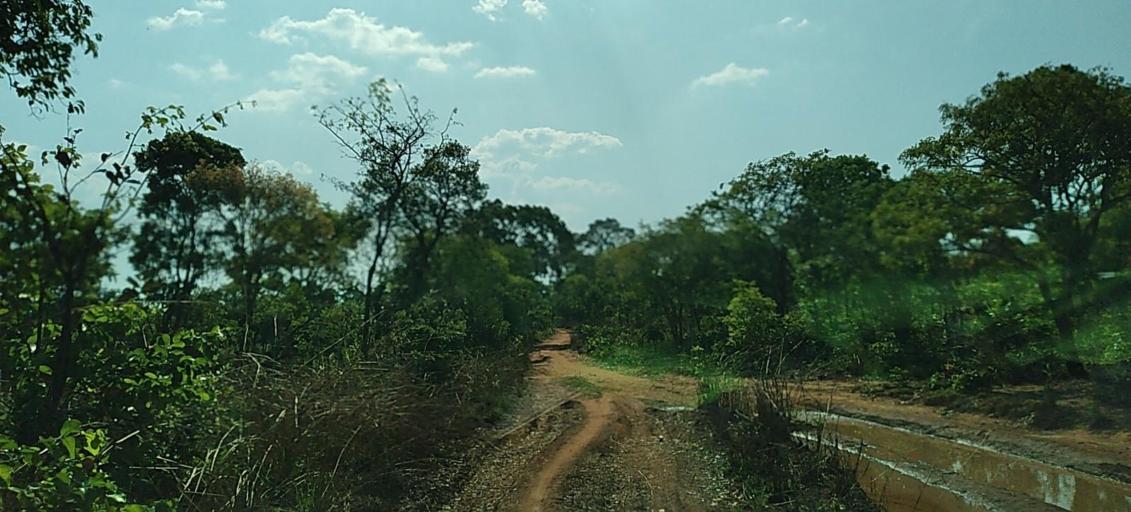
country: ZM
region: North-Western
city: Mwinilunga
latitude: -11.2993
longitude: 24.8691
